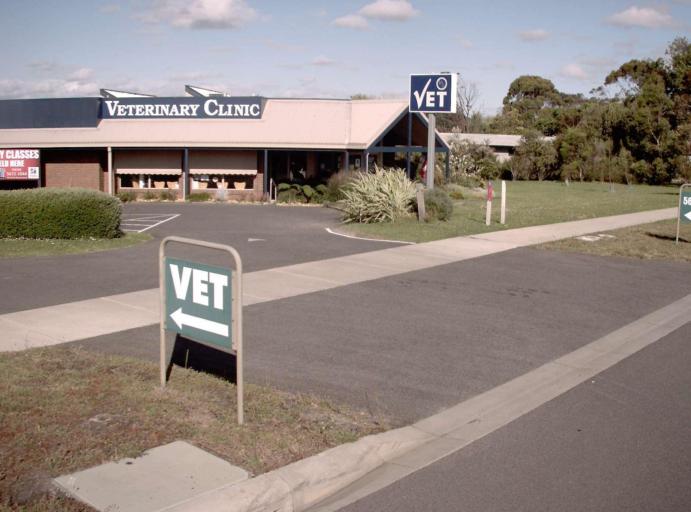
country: AU
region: Victoria
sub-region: Bass Coast
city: North Wonthaggi
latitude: -38.5885
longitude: 145.5806
